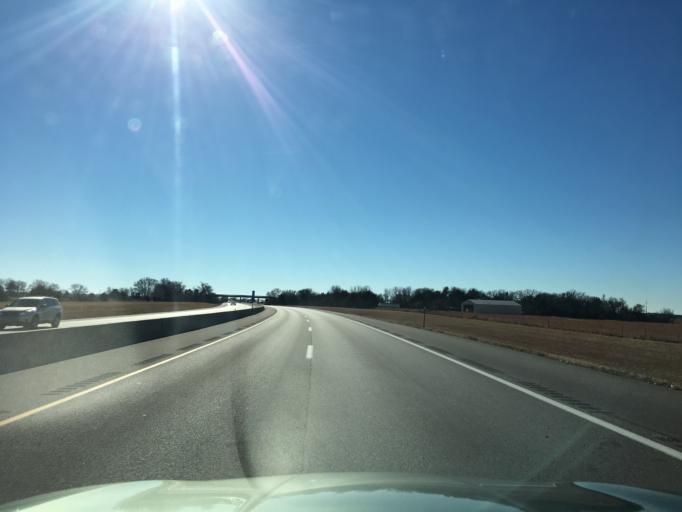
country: US
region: Kansas
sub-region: Sumner County
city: Wellington
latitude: 37.3236
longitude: -97.3395
